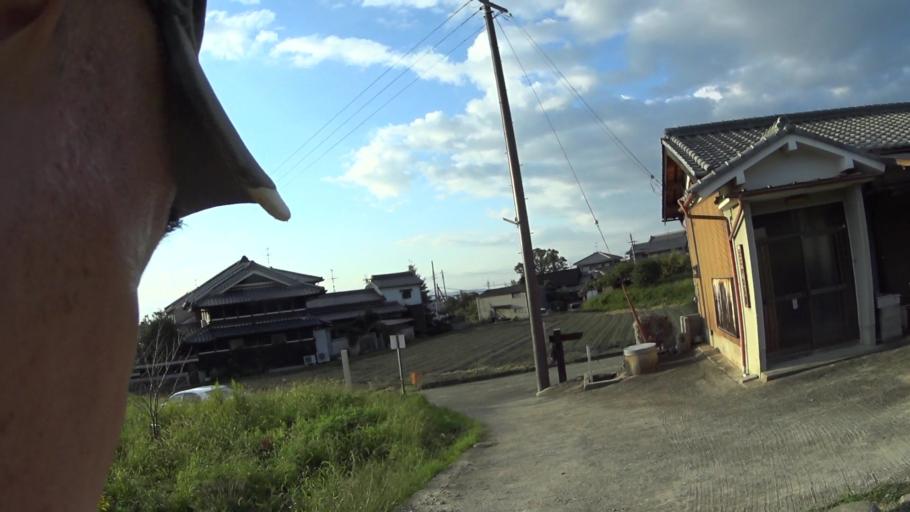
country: JP
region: Nara
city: Tenri
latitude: 34.5527
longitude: 135.8499
